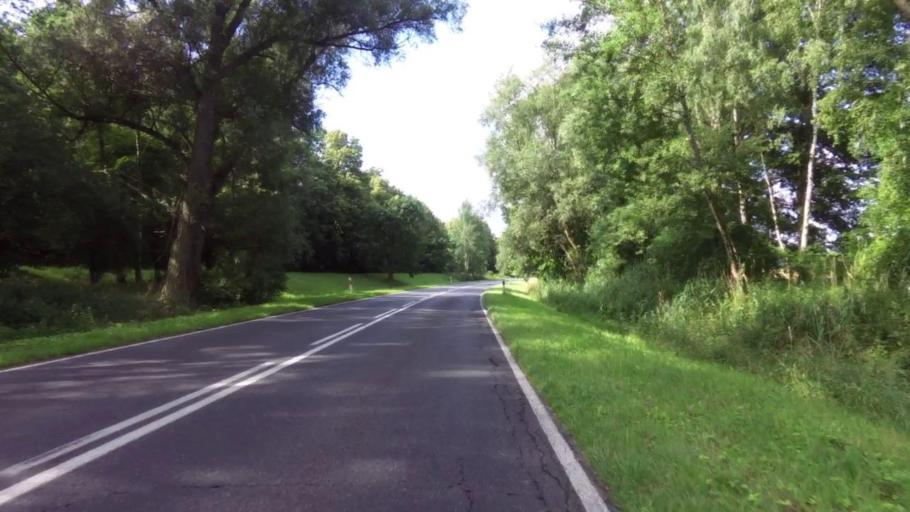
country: PL
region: West Pomeranian Voivodeship
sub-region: Powiat gryfinski
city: Cedynia
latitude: 52.8623
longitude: 14.1790
